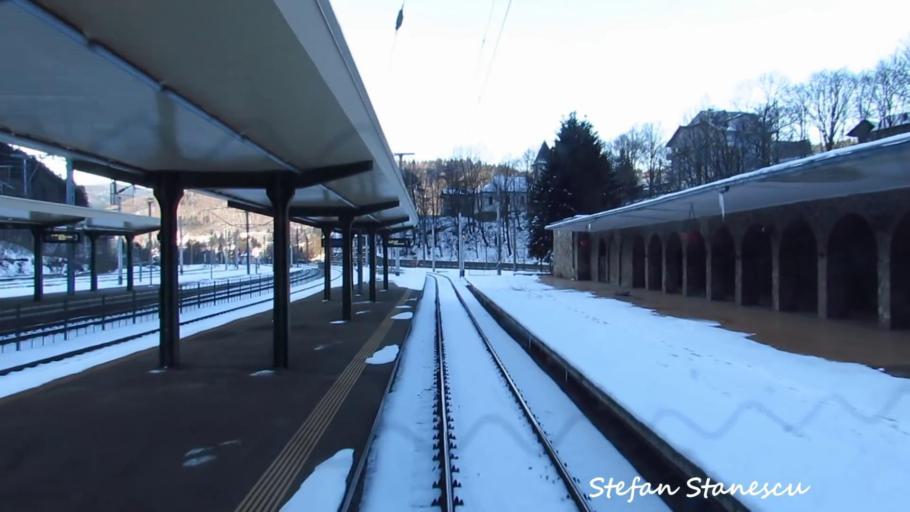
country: RO
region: Prahova
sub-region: Oras Sinaia
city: Sinaia
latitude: 45.3550
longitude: 25.5555
